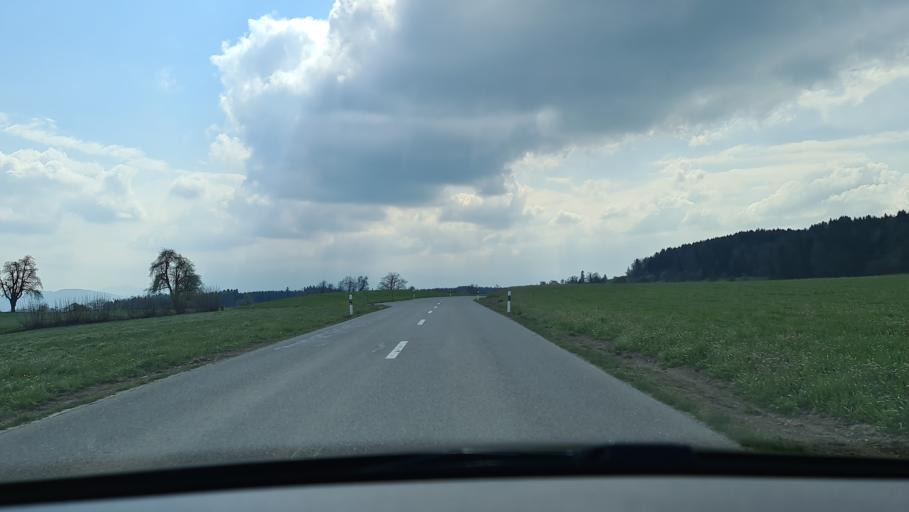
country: CH
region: Lucerne
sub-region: Hochdorf District
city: Ballwil
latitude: 47.1693
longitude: 8.3541
